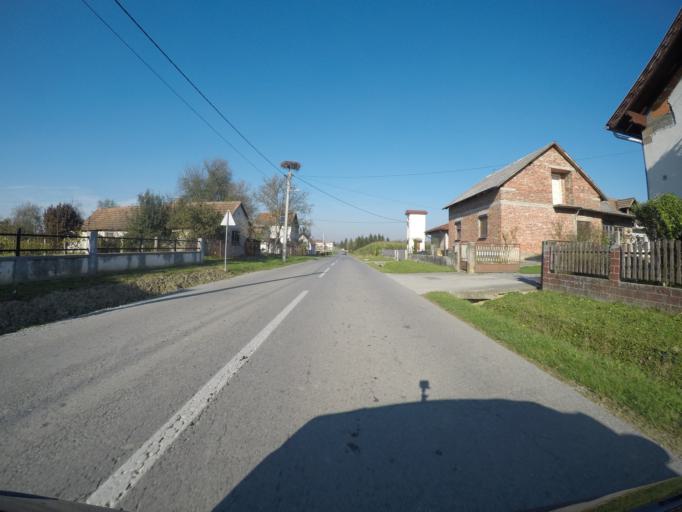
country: HR
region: Bjelovarsko-Bilogorska
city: Predavac
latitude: 45.9161
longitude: 16.7857
